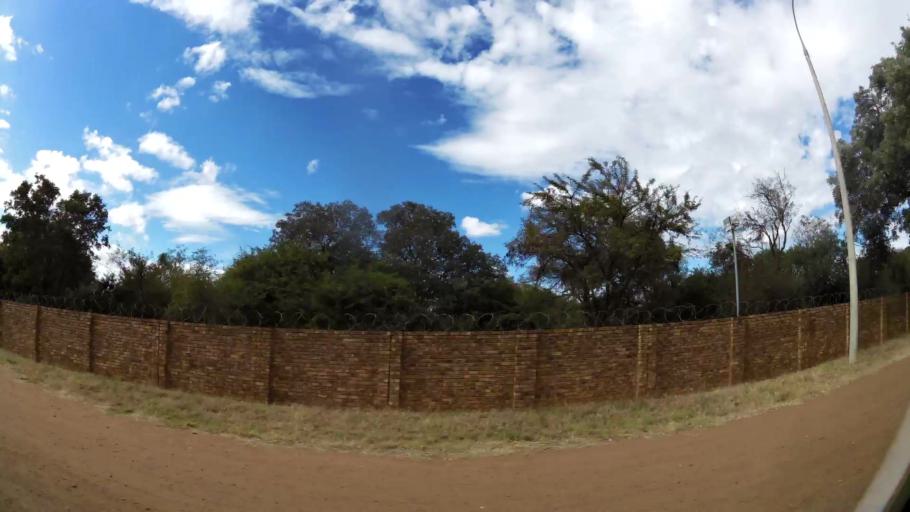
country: ZA
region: Limpopo
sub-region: Waterberg District Municipality
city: Warmbaths
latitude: -24.8912
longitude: 28.2833
